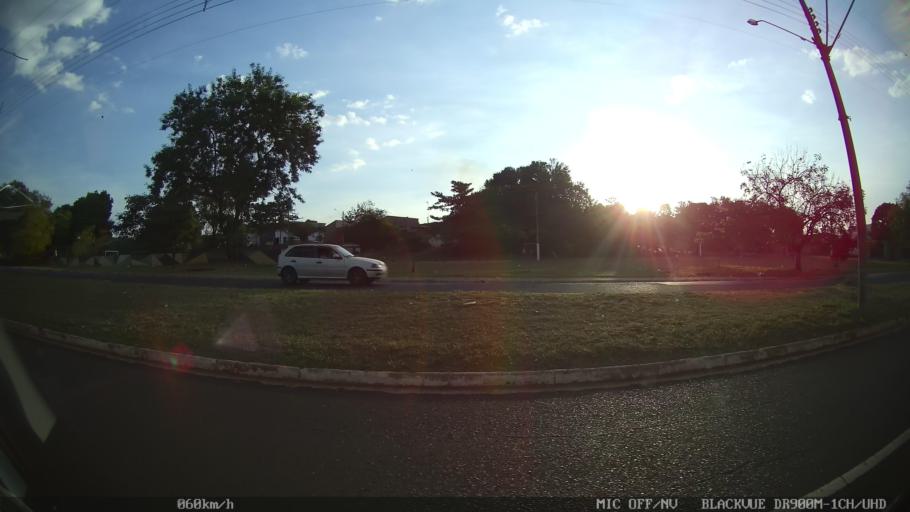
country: BR
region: Sao Paulo
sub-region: Ribeirao Preto
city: Ribeirao Preto
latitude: -21.1308
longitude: -47.8040
